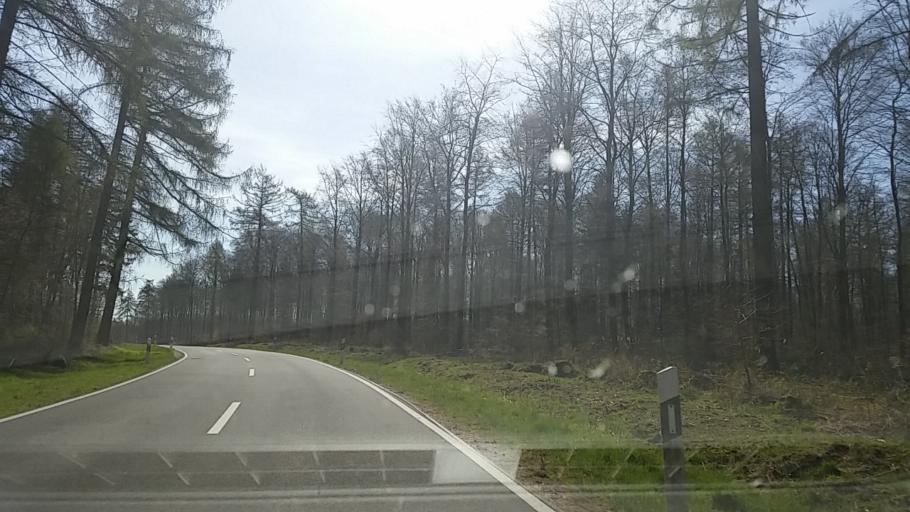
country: DE
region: Lower Saxony
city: Warberg
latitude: 52.1567
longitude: 10.9176
